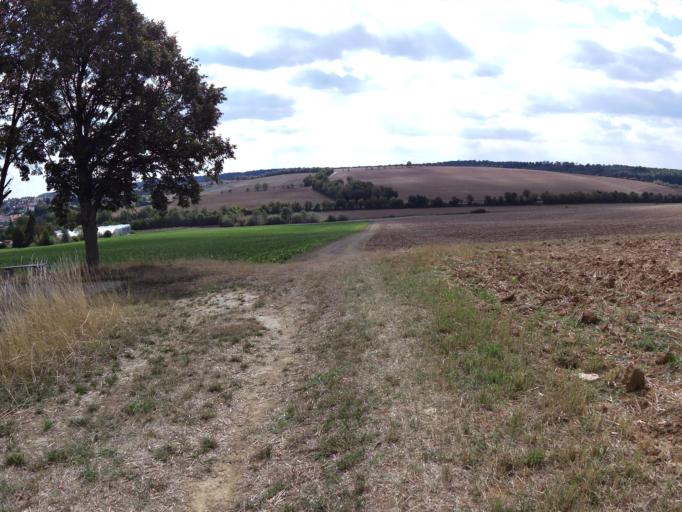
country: DE
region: Bavaria
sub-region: Regierungsbezirk Unterfranken
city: Hettstadt
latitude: 49.7894
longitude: 9.8225
